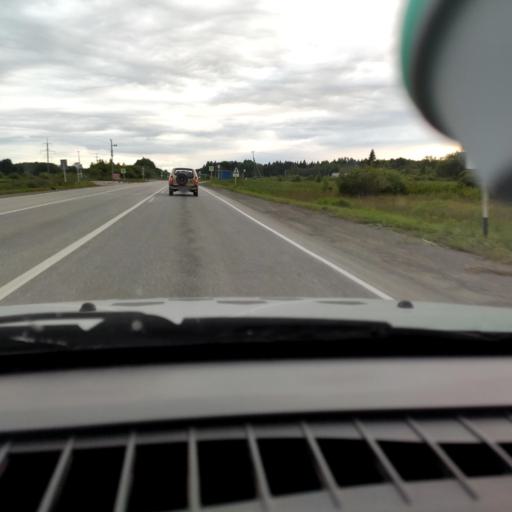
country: RU
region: Perm
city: Kalino
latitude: 58.3254
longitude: 57.6320
